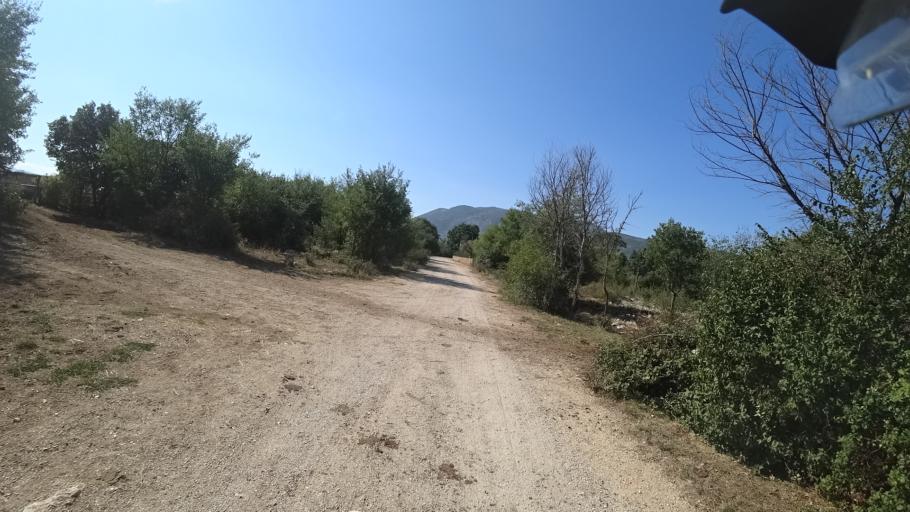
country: HR
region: Sibensko-Kniniska
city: Knin
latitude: 43.9707
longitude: 16.1839
